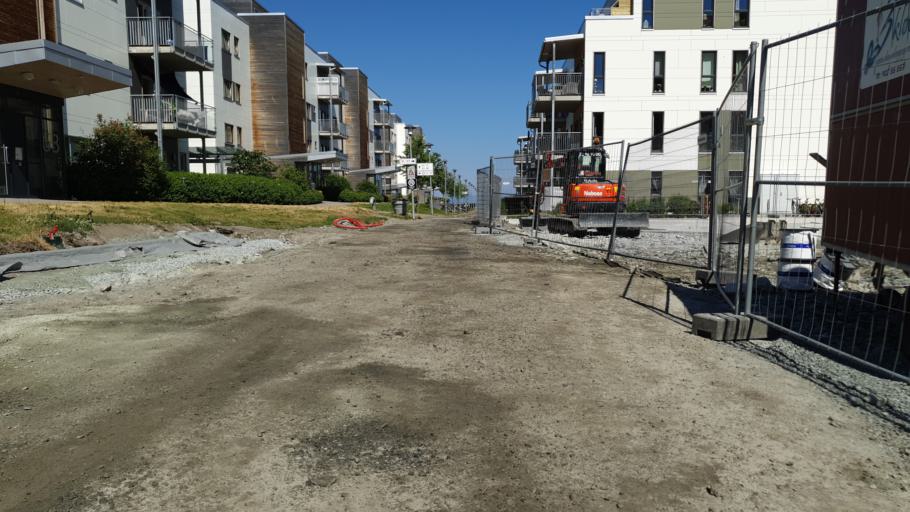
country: NO
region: Sor-Trondelag
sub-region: Trondheim
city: Trondheim
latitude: 63.4291
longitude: 10.5269
